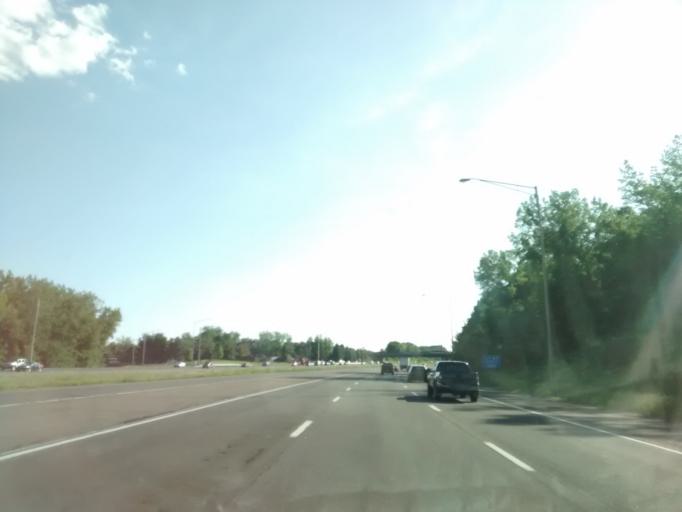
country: US
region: Connecticut
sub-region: Hartford County
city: Manchester
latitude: 41.8142
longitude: -72.5150
